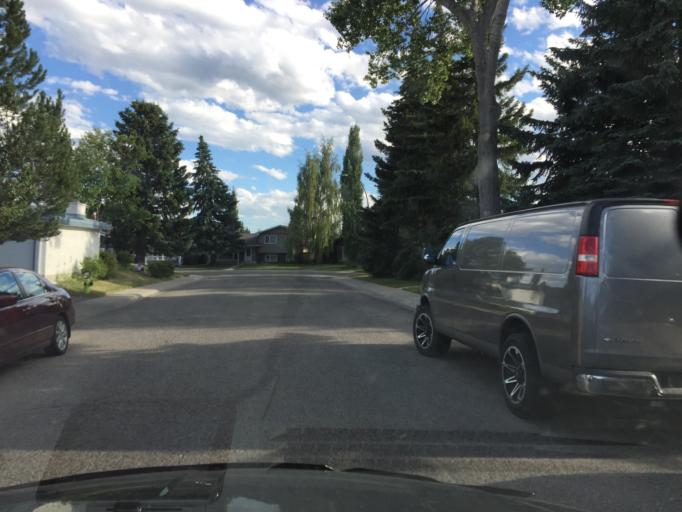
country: CA
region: Alberta
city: Calgary
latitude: 50.9339
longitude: -114.0455
